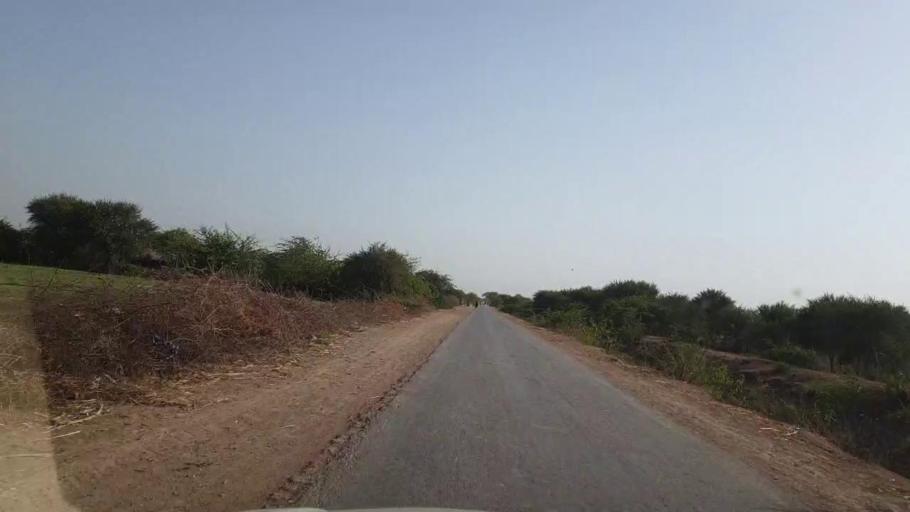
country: PK
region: Sindh
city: Tando Ghulam Ali
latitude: 25.0922
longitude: 68.8689
